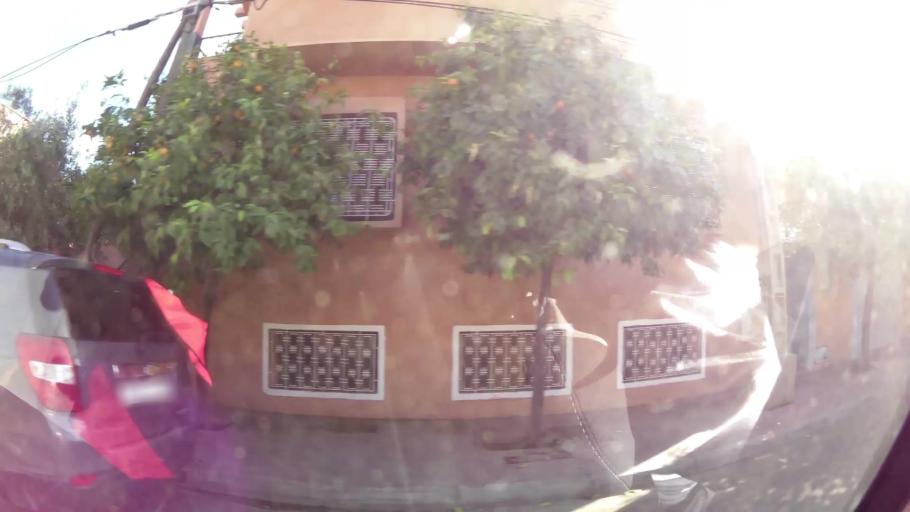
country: MA
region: Marrakech-Tensift-Al Haouz
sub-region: Marrakech
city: Marrakesh
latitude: 31.6548
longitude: -8.0076
